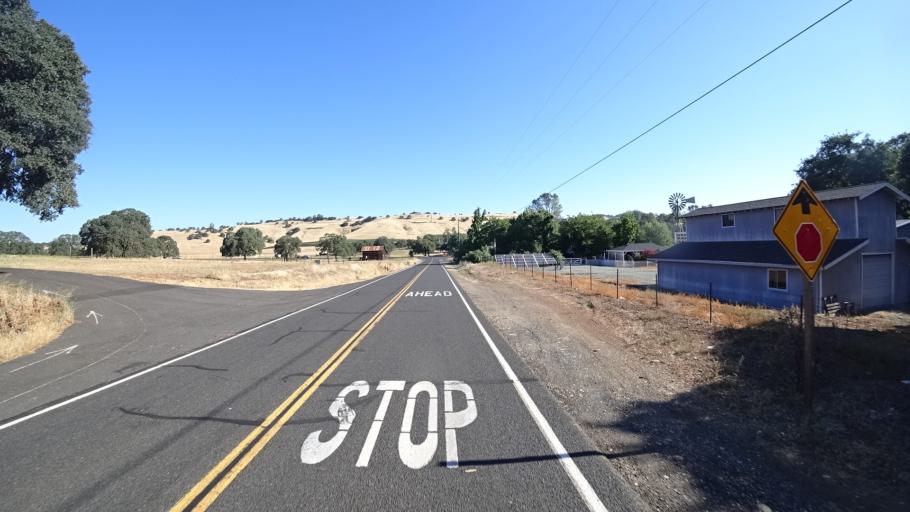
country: US
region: California
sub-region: Calaveras County
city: Murphys
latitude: 38.0917
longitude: -120.4850
